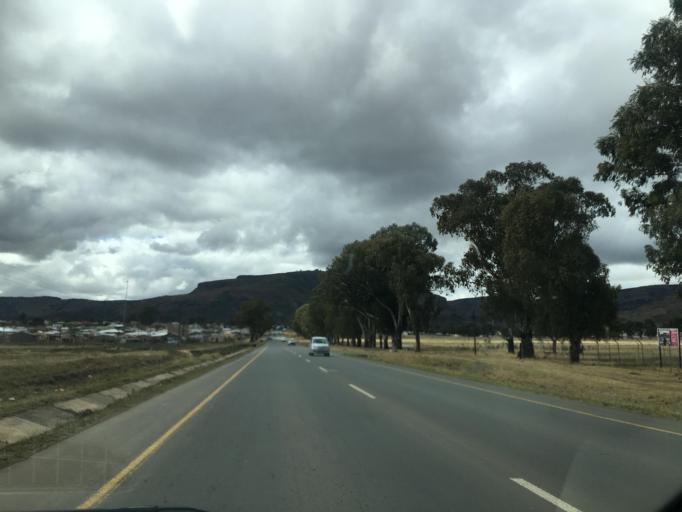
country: ZA
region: Eastern Cape
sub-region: Chris Hani District Municipality
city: Cala
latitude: -31.5295
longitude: 27.6807
